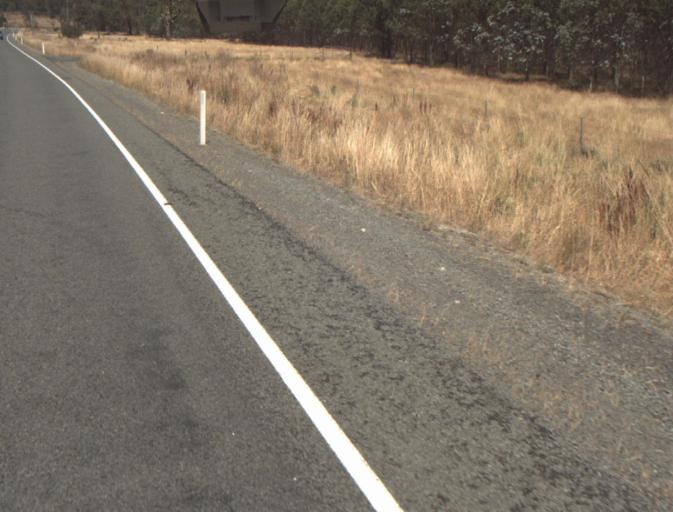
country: AU
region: Tasmania
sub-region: Launceston
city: Newstead
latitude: -41.3533
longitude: 147.3390
